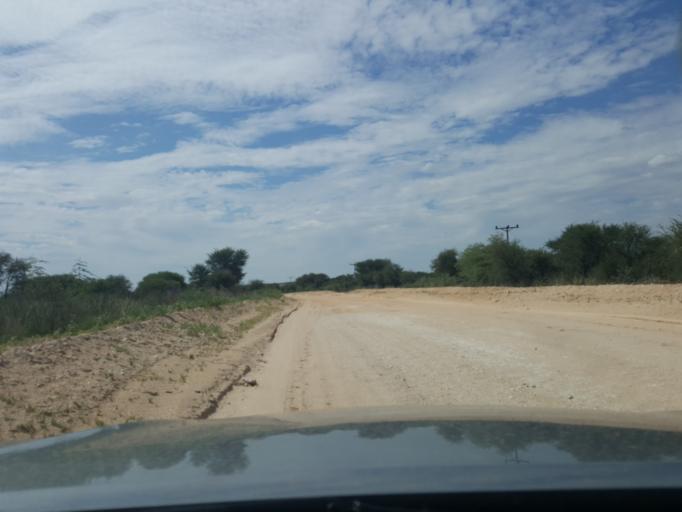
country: BW
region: Kweneng
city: Letlhakeng
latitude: -24.0633
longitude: 25.0309
